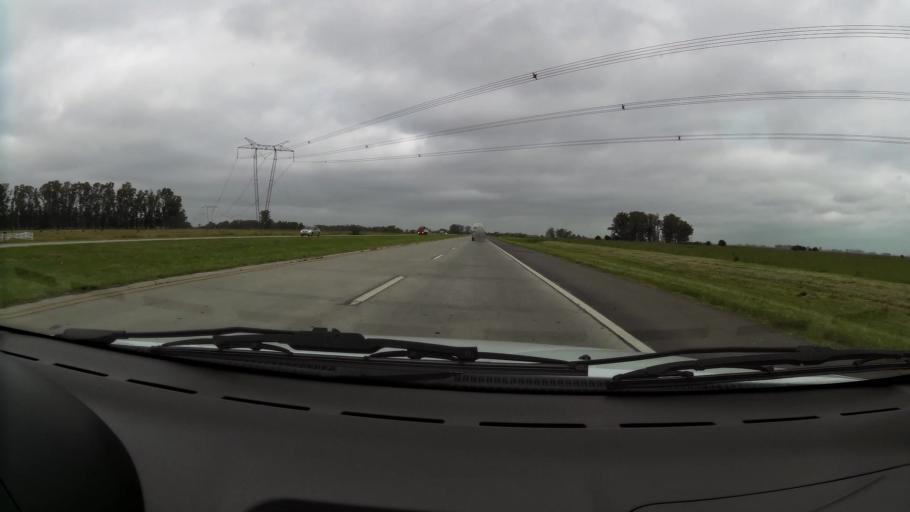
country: AR
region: Buenos Aires
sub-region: Partido de Brandsen
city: Brandsen
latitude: -35.0248
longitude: -58.2410
